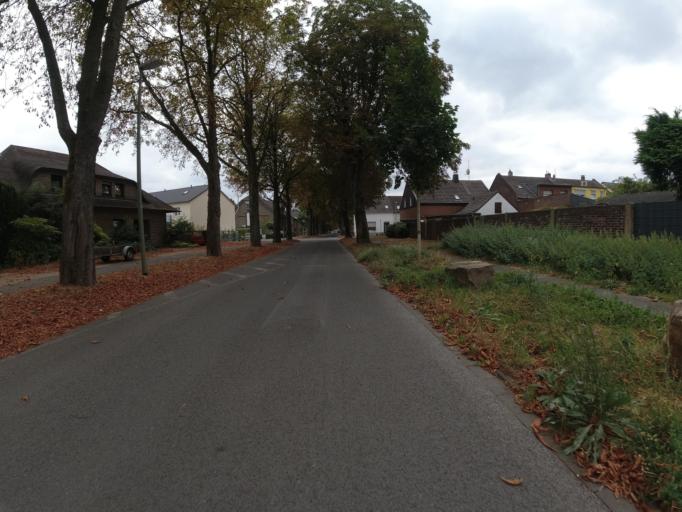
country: DE
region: North Rhine-Westphalia
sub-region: Regierungsbezirk Dusseldorf
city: Moers
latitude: 51.4545
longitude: 6.6811
